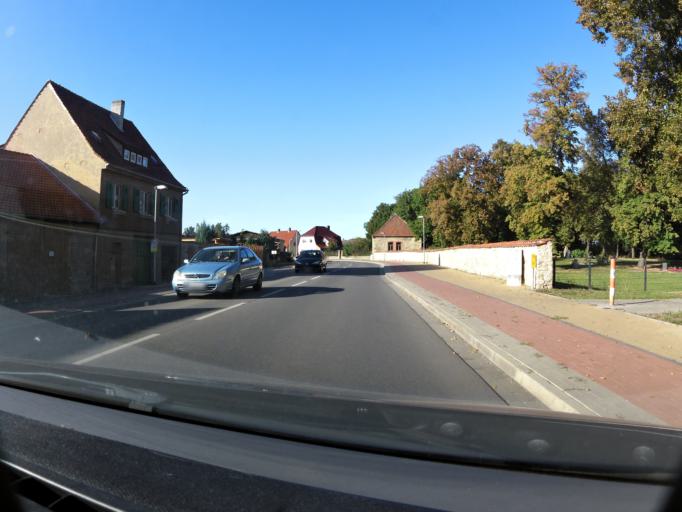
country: DE
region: Saxony-Anhalt
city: Groeningen
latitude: 51.9409
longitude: 11.2203
